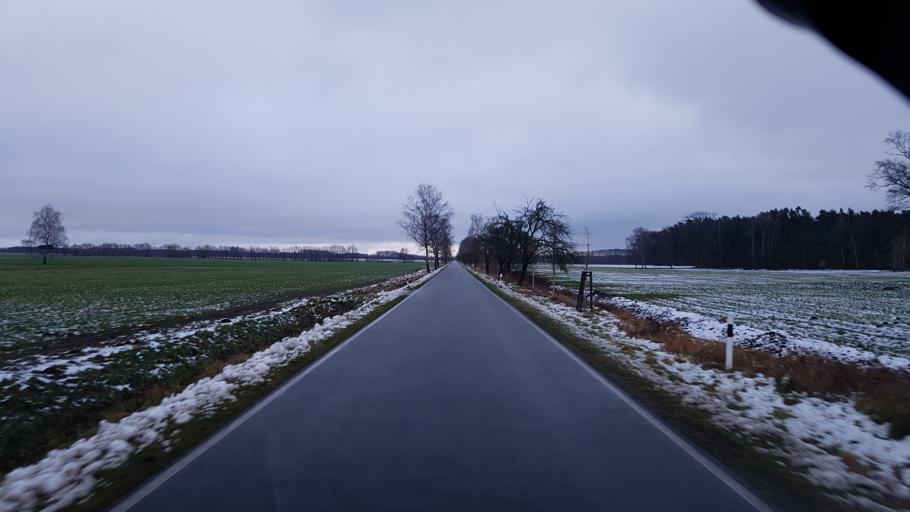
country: DE
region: Brandenburg
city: Luckau
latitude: 51.8147
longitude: 13.7040
